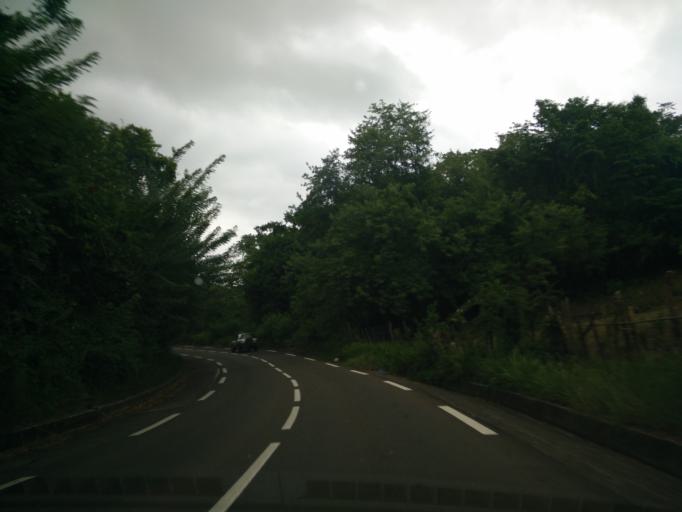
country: MQ
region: Martinique
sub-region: Martinique
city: Le Marin
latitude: 14.4991
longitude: -60.8541
